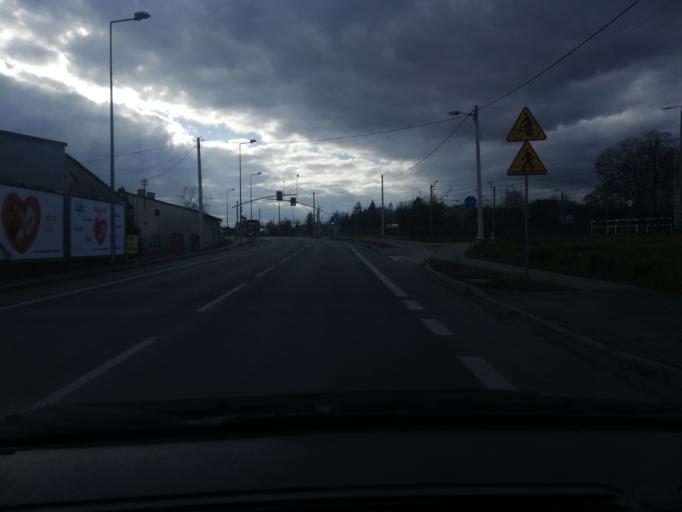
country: PL
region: Silesian Voivodeship
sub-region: Czestochowa
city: Czestochowa
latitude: 50.8289
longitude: 19.1393
